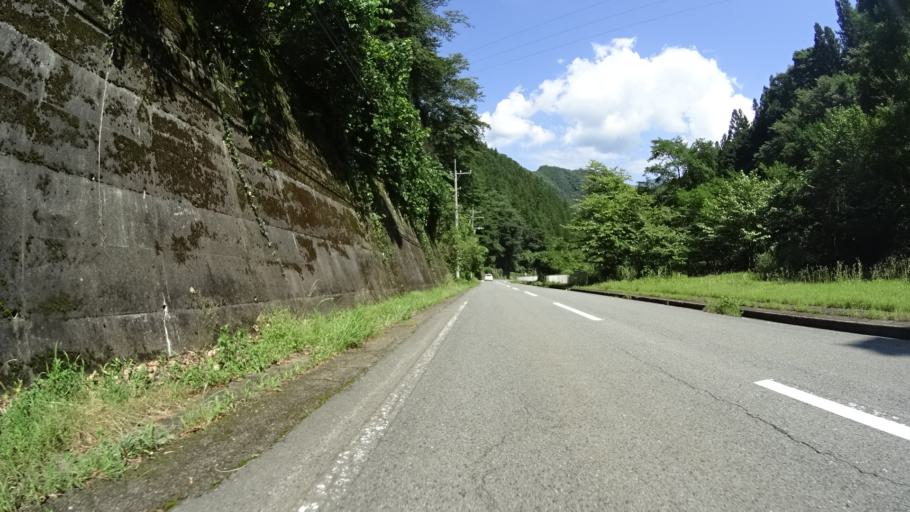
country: JP
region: Gunma
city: Tomioka
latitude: 36.0766
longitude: 138.8255
